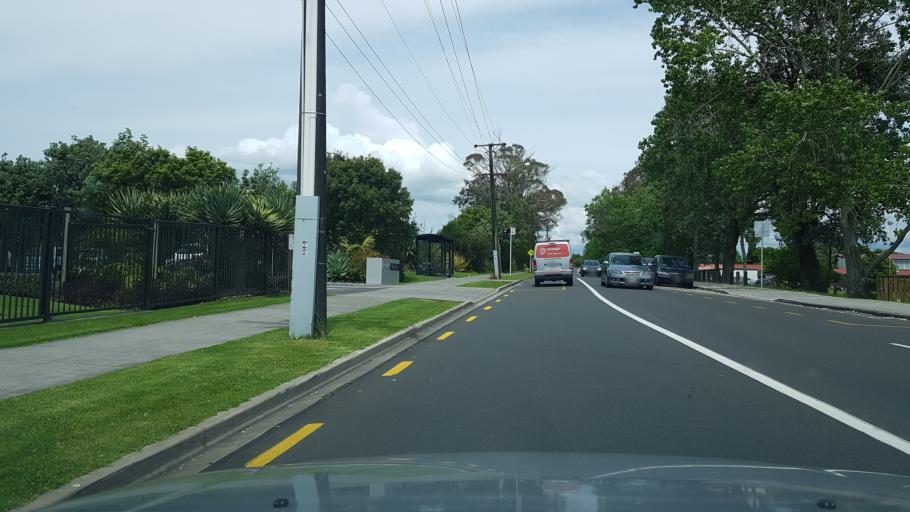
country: NZ
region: Auckland
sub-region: Auckland
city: North Shore
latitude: -36.7964
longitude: 174.7539
